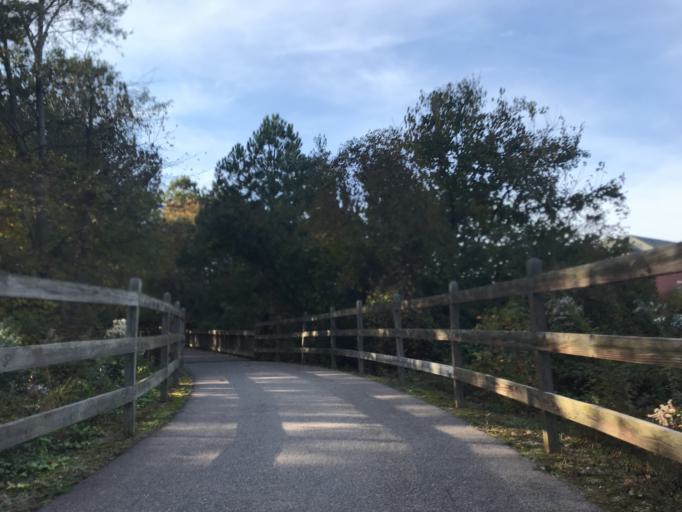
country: US
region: North Carolina
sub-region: Wake County
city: West Raleigh
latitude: 35.7950
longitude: -78.6903
